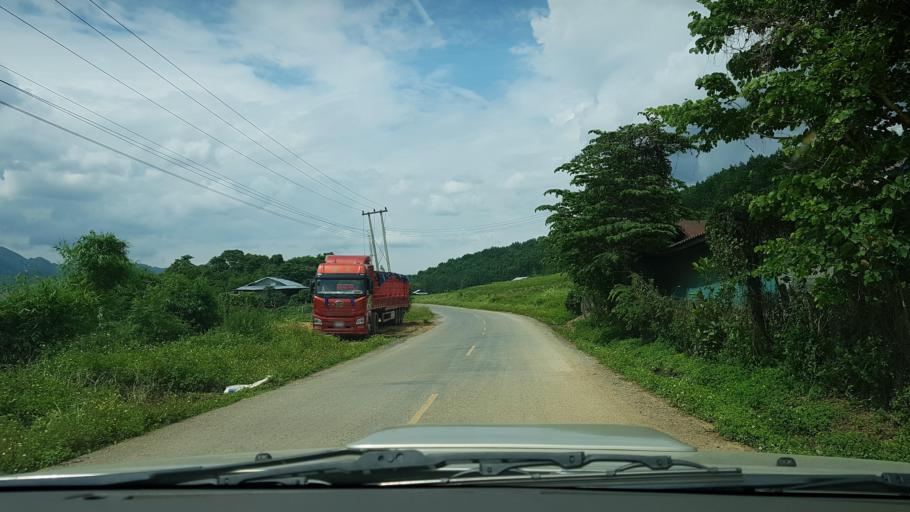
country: LA
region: Loungnamtha
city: Muang Nale
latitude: 20.2586
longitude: 101.5910
